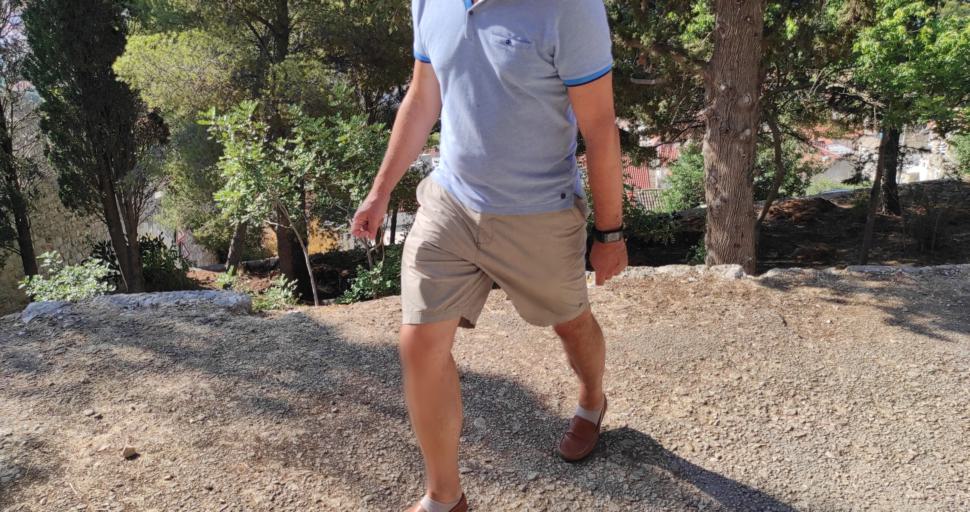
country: HR
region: Splitsko-Dalmatinska
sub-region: Grad Hvar
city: Hvar
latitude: 43.1740
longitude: 16.4434
